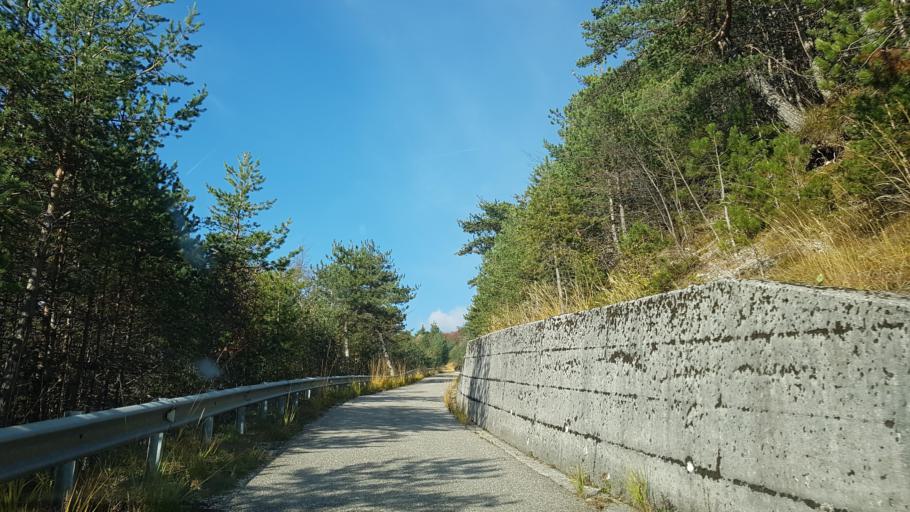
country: IT
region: Friuli Venezia Giulia
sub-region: Provincia di Udine
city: Moggio Udinese
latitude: 46.4475
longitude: 13.2027
